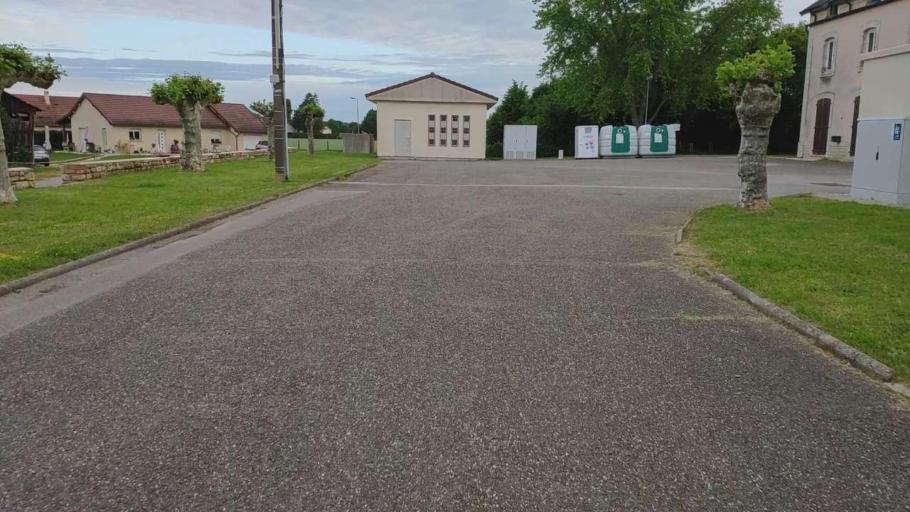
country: FR
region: Franche-Comte
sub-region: Departement du Jura
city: Bletterans
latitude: 46.7485
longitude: 5.4615
